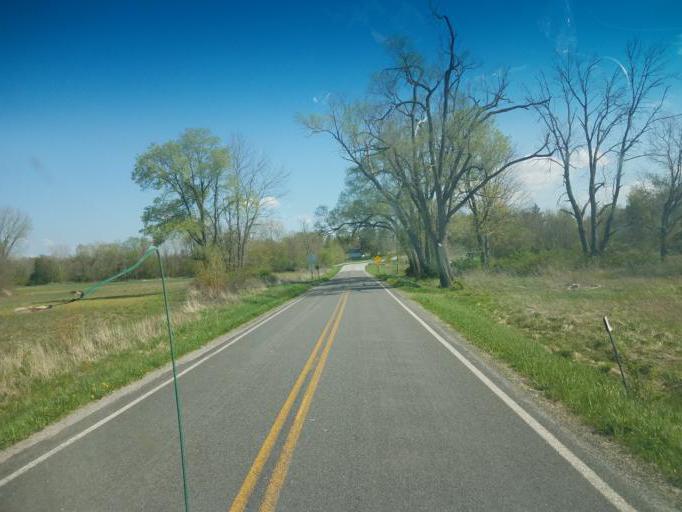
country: US
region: Ohio
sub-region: Medina County
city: Westfield Center
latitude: 40.9906
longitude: -81.9406
